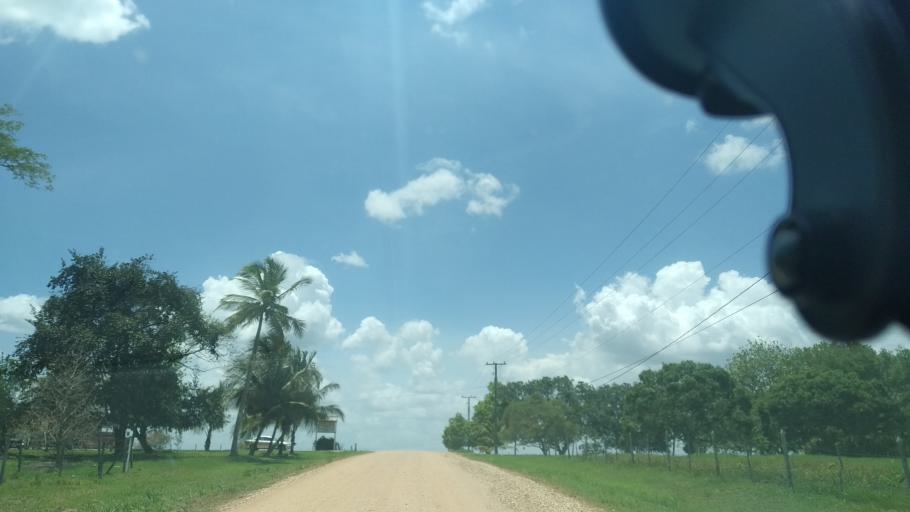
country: BZ
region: Cayo
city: San Ignacio
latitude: 17.2423
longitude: -88.9874
